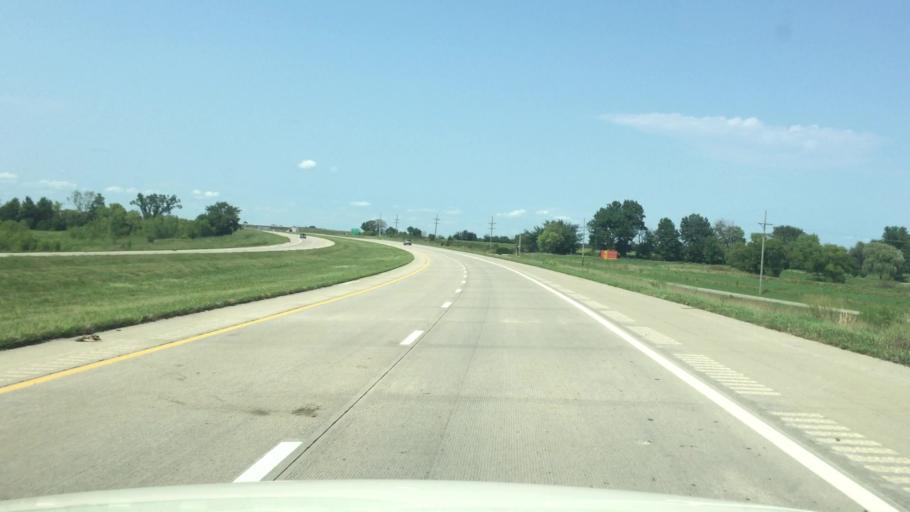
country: US
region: Kansas
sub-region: Linn County
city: Pleasanton
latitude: 38.1579
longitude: -94.6964
